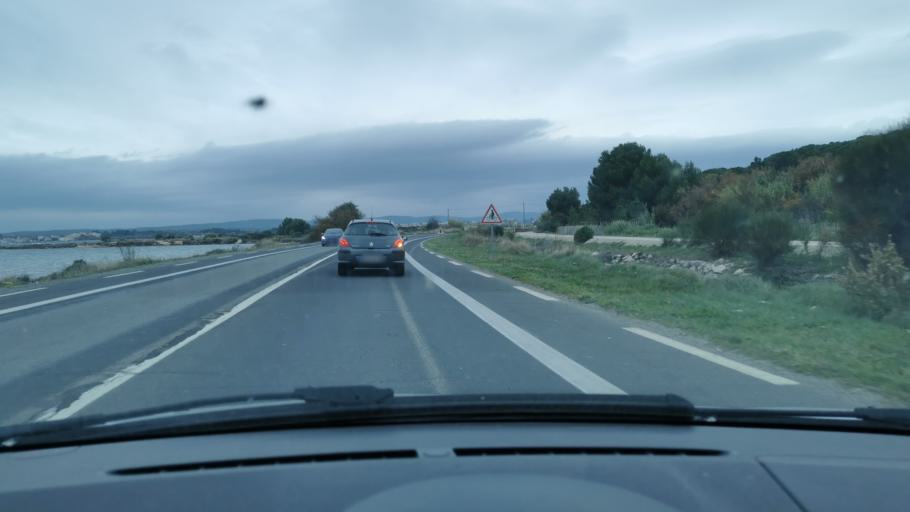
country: FR
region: Languedoc-Roussillon
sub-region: Departement de l'Herault
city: Balaruc-les-Bains
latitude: 43.4316
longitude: 3.7037
